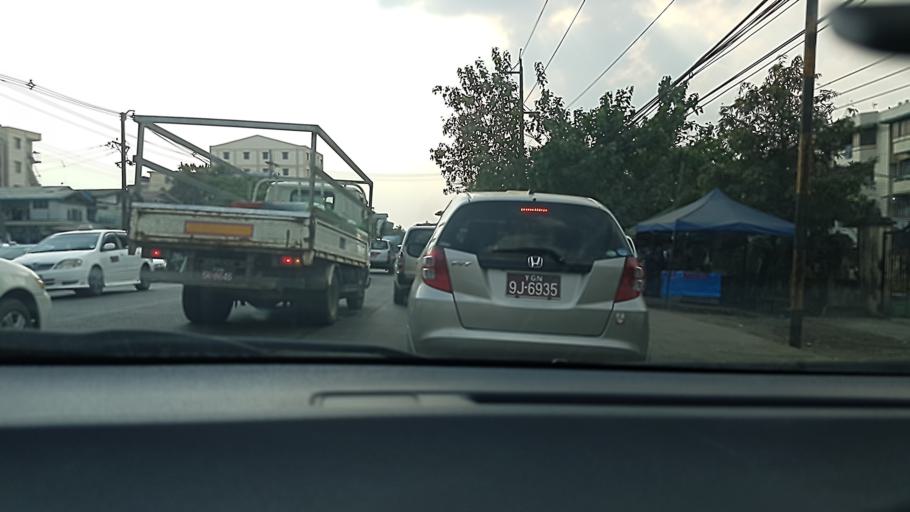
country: MM
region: Yangon
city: Syriam
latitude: 16.8053
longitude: 96.2143
